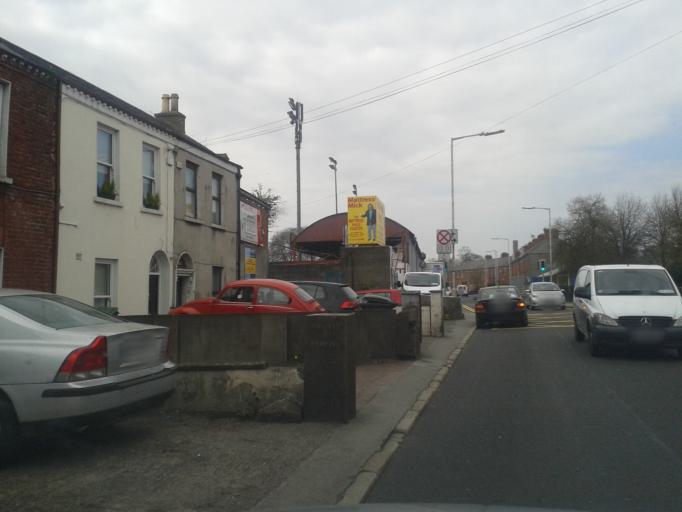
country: IE
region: Leinster
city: Drumcondra
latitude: 53.3672
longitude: -6.2503
